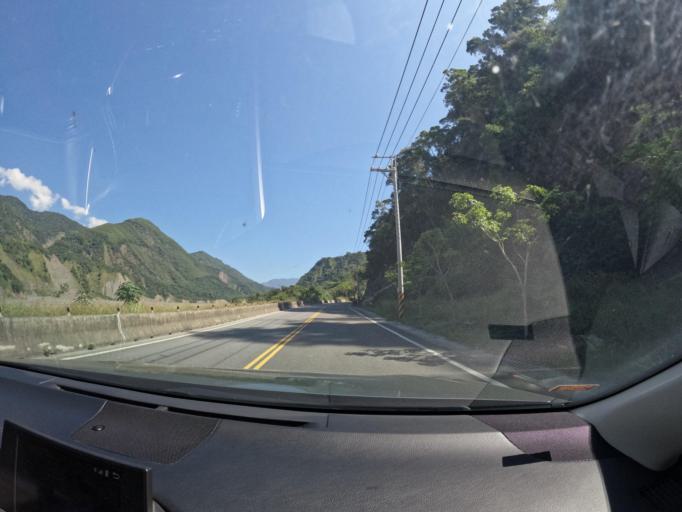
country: TW
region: Taiwan
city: Yujing
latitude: 23.1757
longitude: 120.7785
